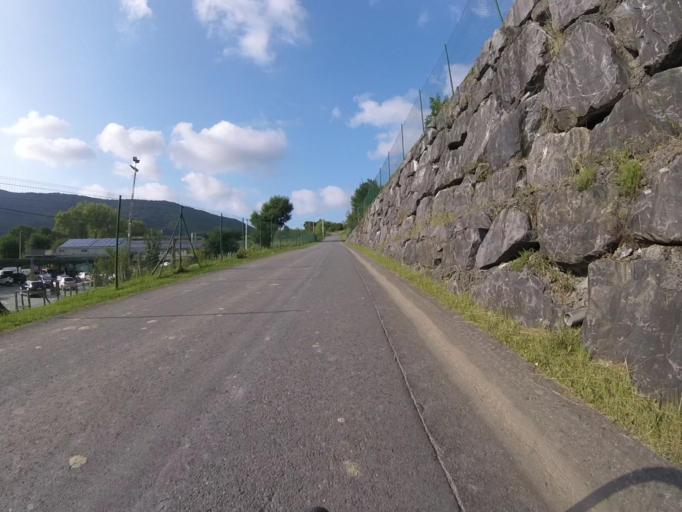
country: ES
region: Basque Country
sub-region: Provincia de Guipuzcoa
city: Irun
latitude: 43.3469
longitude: -1.8196
